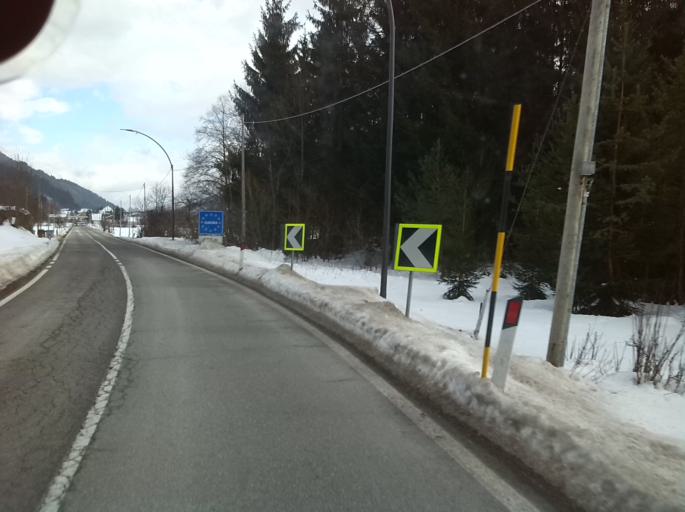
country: AT
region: Carinthia
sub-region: Politischer Bezirk Villach Land
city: Arnoldstein
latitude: 46.4976
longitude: 13.6960
